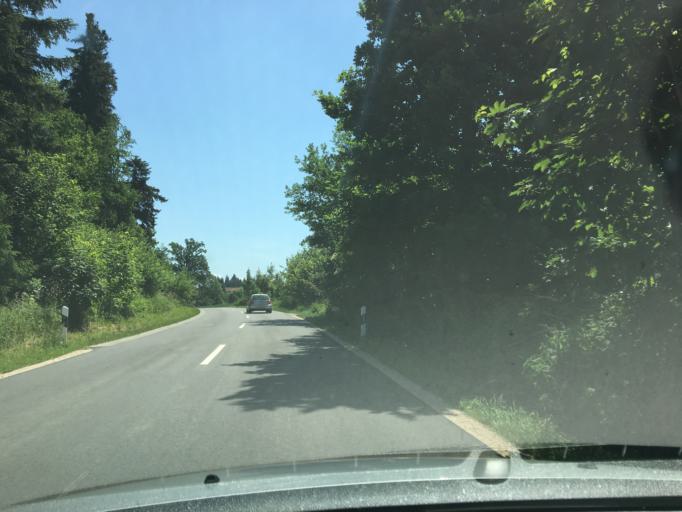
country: DE
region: Bavaria
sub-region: Upper Bavaria
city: Halsbach
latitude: 48.1133
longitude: 12.6809
